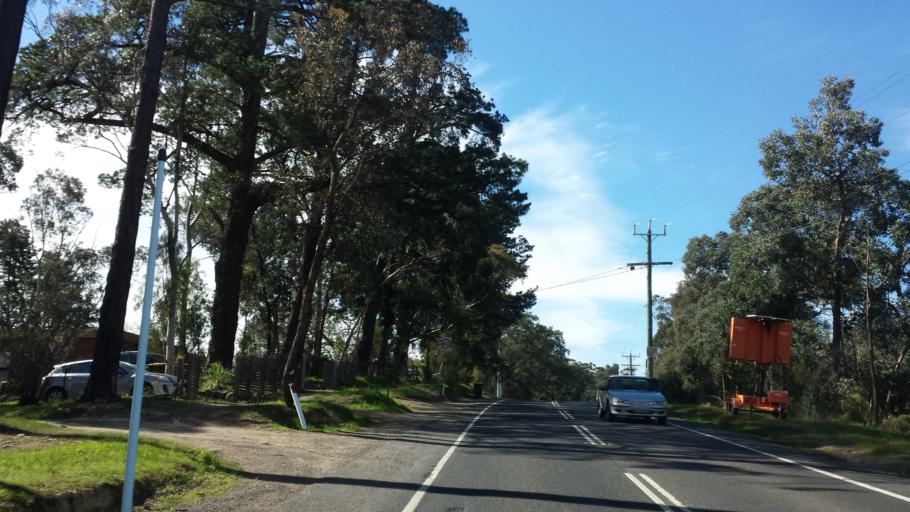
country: AU
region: Victoria
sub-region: Nillumbik
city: North Warrandyte
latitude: -37.7310
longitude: 145.2279
